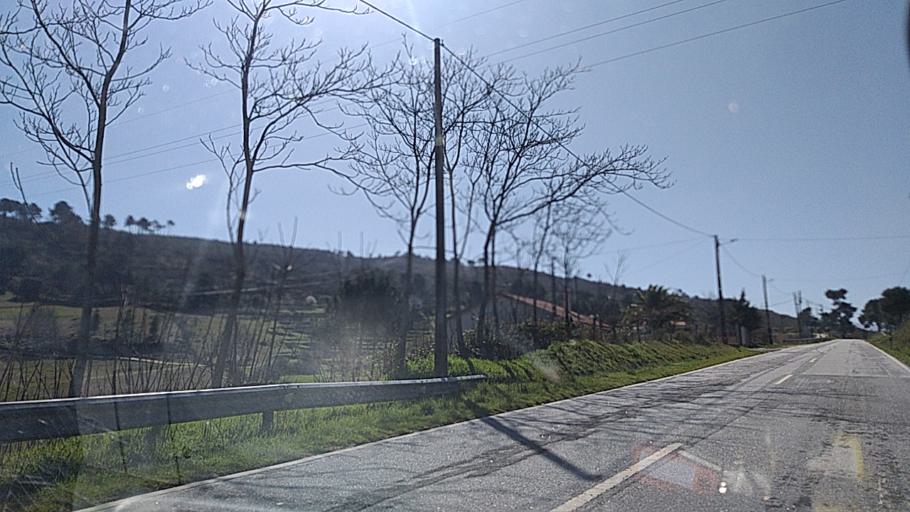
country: PT
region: Guarda
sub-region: Celorico da Beira
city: Celorico da Beira
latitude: 40.6099
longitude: -7.4164
